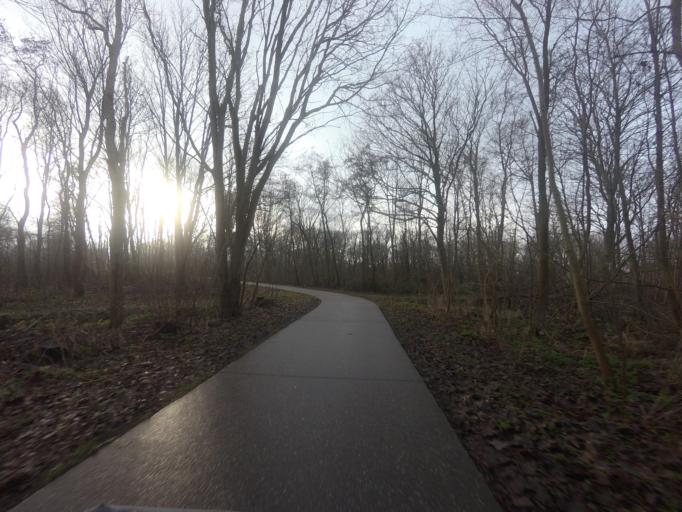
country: NL
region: North Holland
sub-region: Gemeente Texel
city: Den Burg
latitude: 53.1571
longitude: 4.8478
